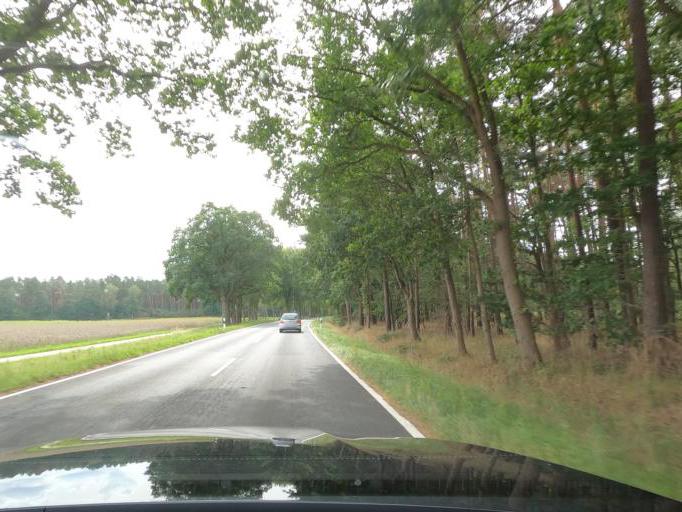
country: DE
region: Lower Saxony
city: Burgdorf
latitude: 52.5064
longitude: 9.9699
